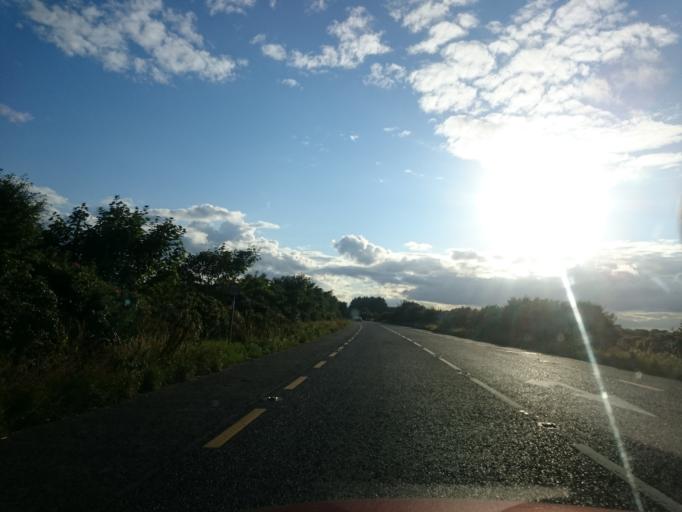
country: IE
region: Leinster
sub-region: Loch Garman
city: Ballygerry
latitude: 52.2448
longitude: -6.3729
